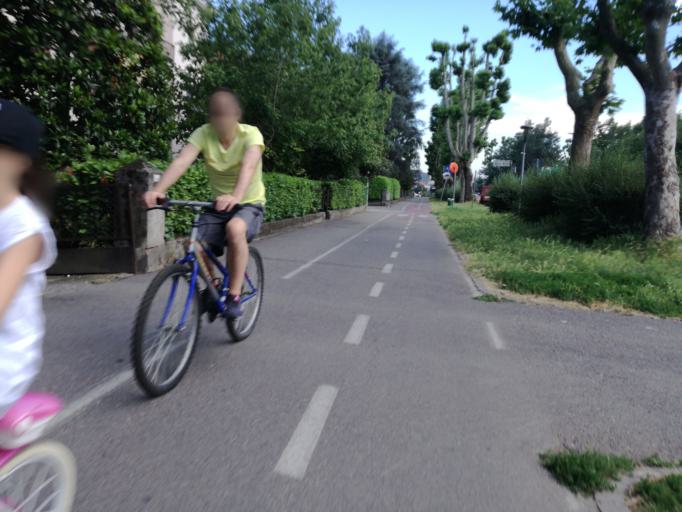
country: IT
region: Piedmont
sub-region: Provincia di Novara
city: Novara
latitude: 45.4367
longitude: 8.6196
